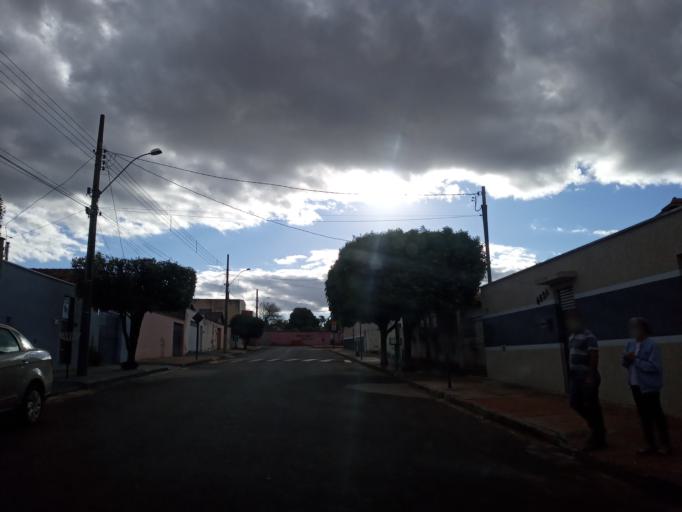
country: BR
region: Minas Gerais
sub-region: Ituiutaba
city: Ituiutaba
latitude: -18.9835
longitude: -49.4796
